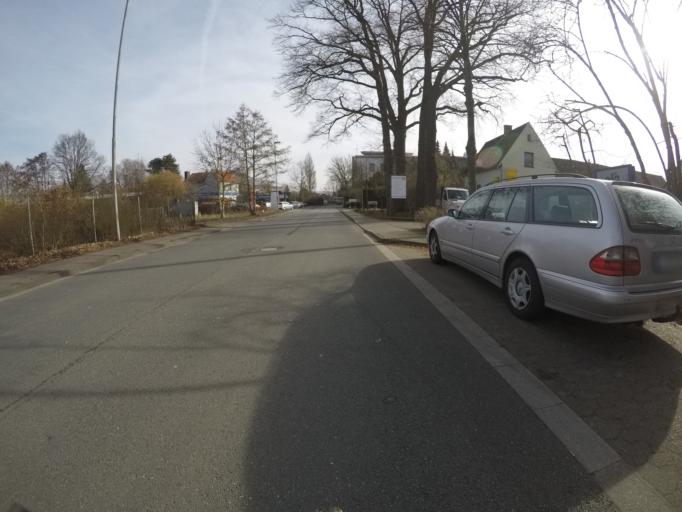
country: DE
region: North Rhine-Westphalia
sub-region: Regierungsbezirk Detmold
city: Herford
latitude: 52.1265
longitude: 8.6461
